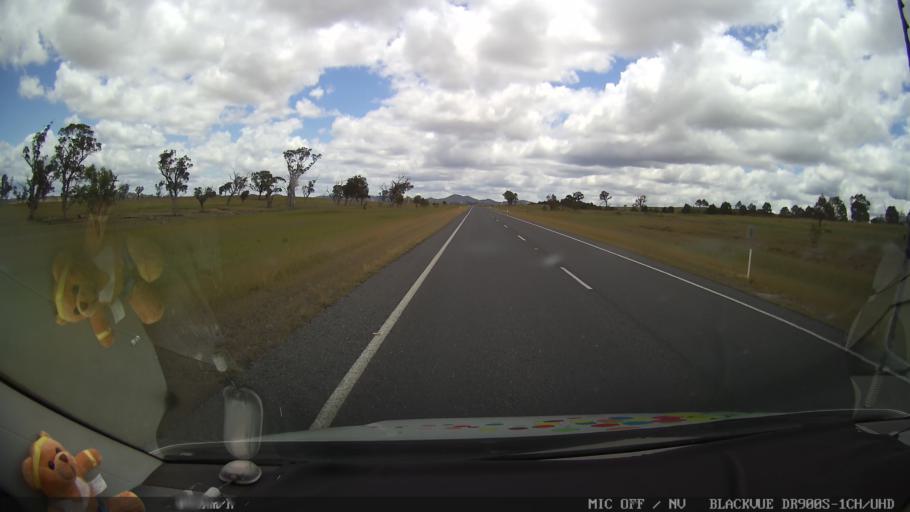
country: AU
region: New South Wales
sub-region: Glen Innes Severn
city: Glen Innes
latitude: -29.4075
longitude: 151.8701
